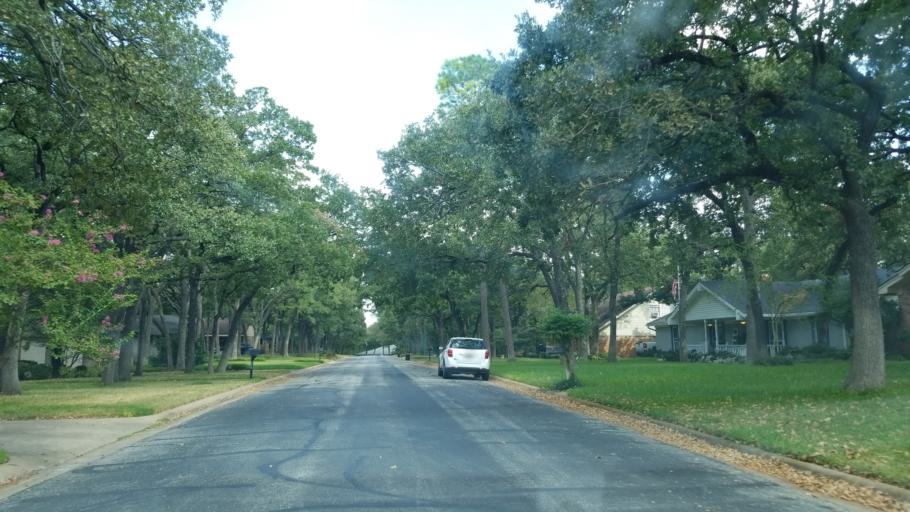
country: US
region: Texas
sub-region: Tarrant County
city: Euless
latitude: 32.8631
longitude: -97.0859
